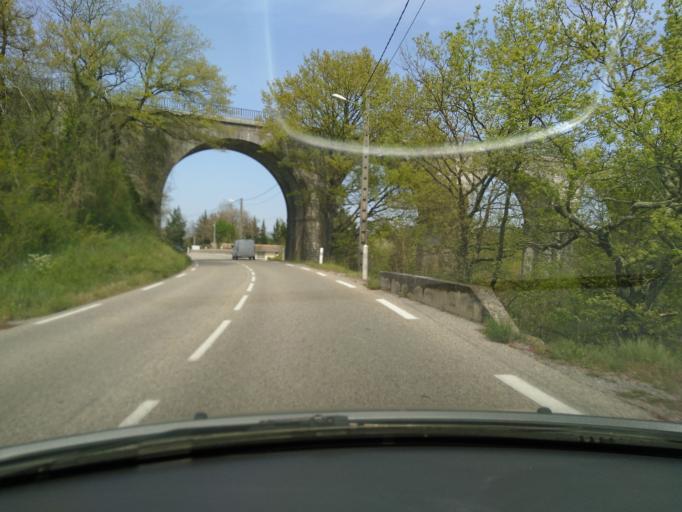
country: FR
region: Rhone-Alpes
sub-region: Departement de l'Ardeche
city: Lavilledieu
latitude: 44.5628
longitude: 4.4609
